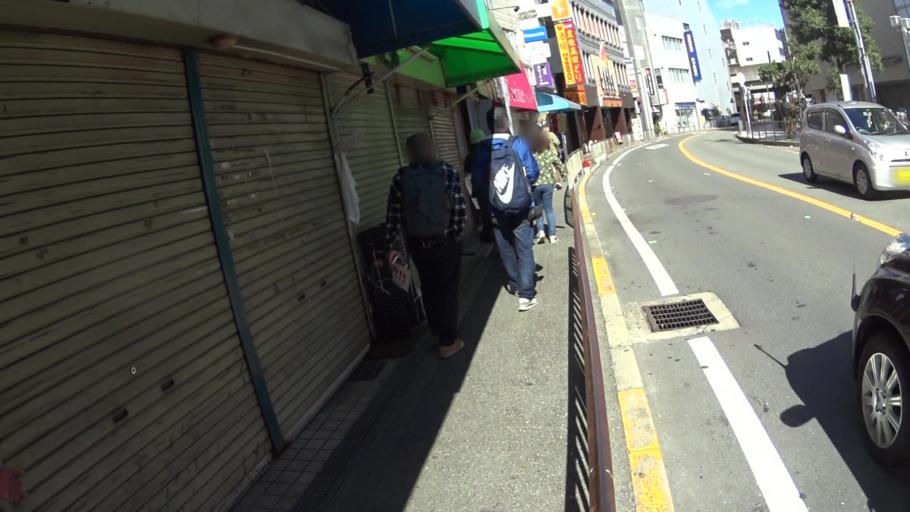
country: JP
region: Osaka
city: Ikeda
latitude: 34.8212
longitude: 135.4245
